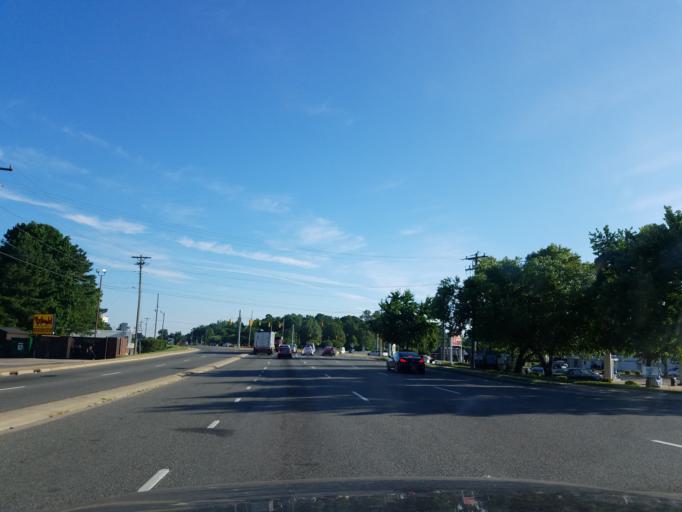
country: US
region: North Carolina
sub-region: Durham County
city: Durham
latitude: 35.9478
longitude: -78.8376
